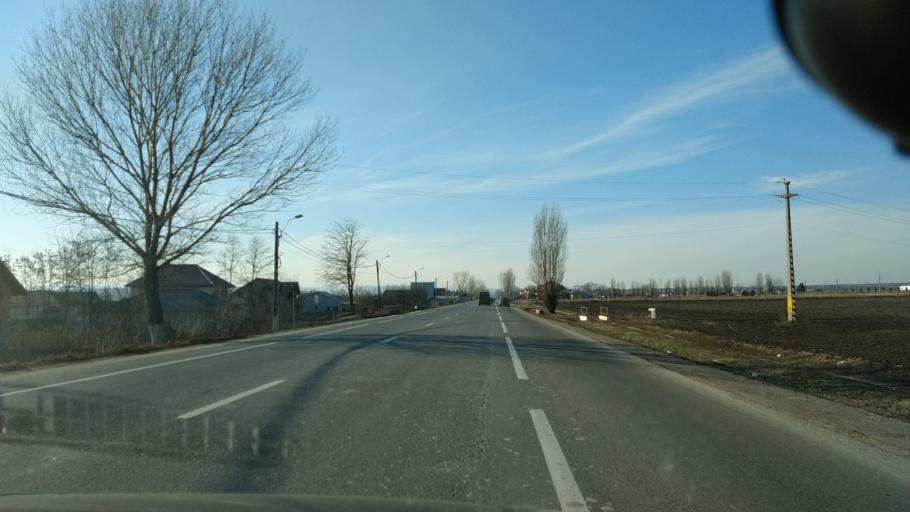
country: RO
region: Iasi
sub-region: Comuna Ion Neculce
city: Razboieni
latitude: 47.2201
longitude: 27.0687
